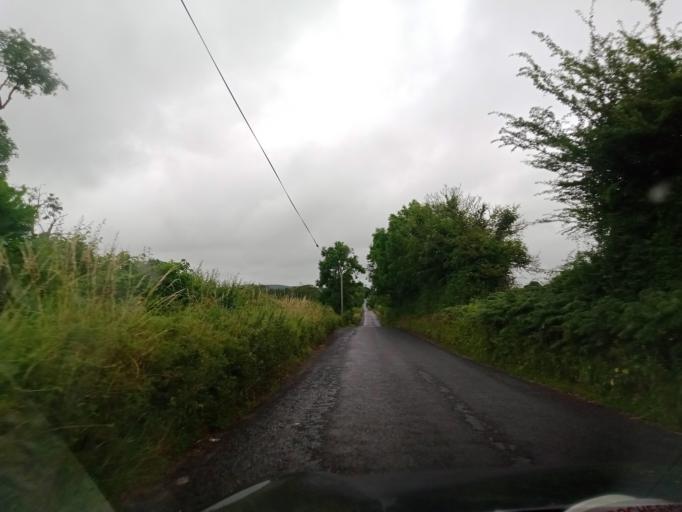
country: IE
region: Leinster
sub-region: Laois
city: Abbeyleix
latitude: 52.9131
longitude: -7.2927
